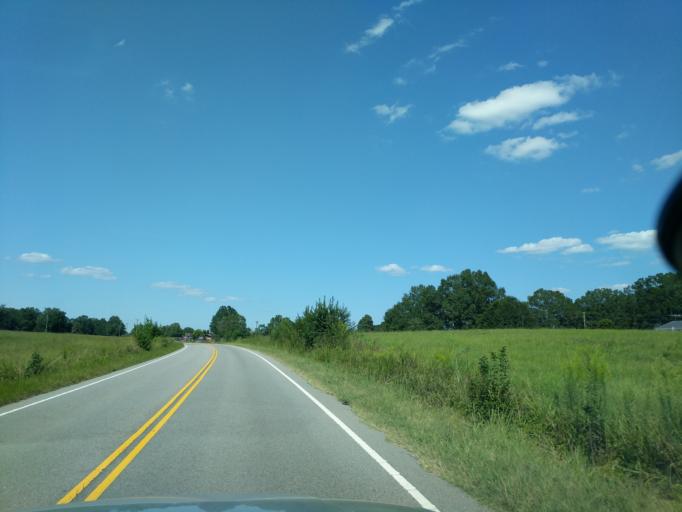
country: US
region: South Carolina
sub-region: Newberry County
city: Prosperity
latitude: 34.1283
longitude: -81.5426
